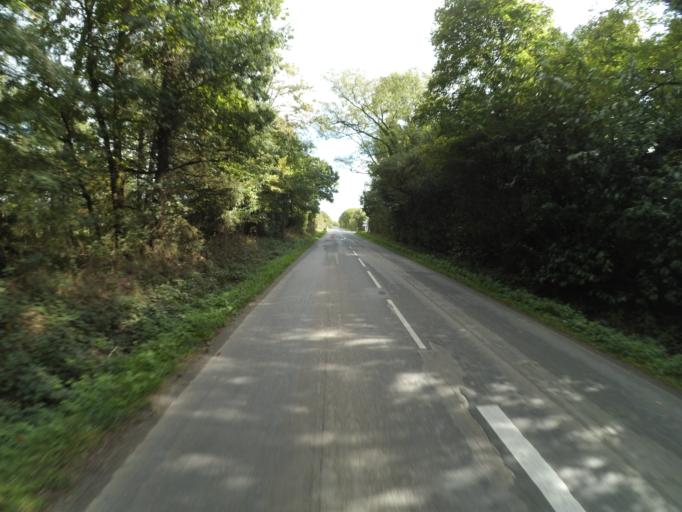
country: FR
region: Pays de la Loire
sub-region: Departement de la Loire-Atlantique
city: Casson
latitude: 47.4028
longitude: -1.5846
